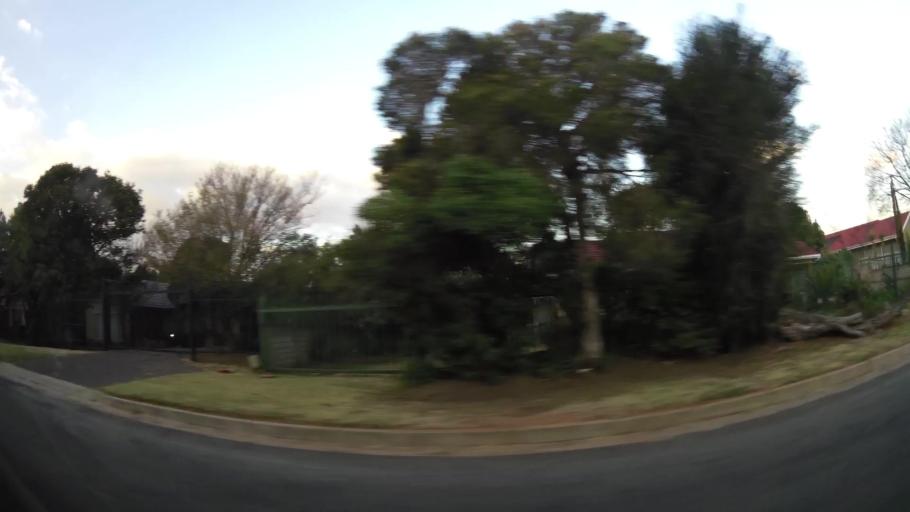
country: ZA
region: Gauteng
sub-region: West Rand District Municipality
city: Krugersdorp
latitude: -26.0742
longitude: 27.7837
